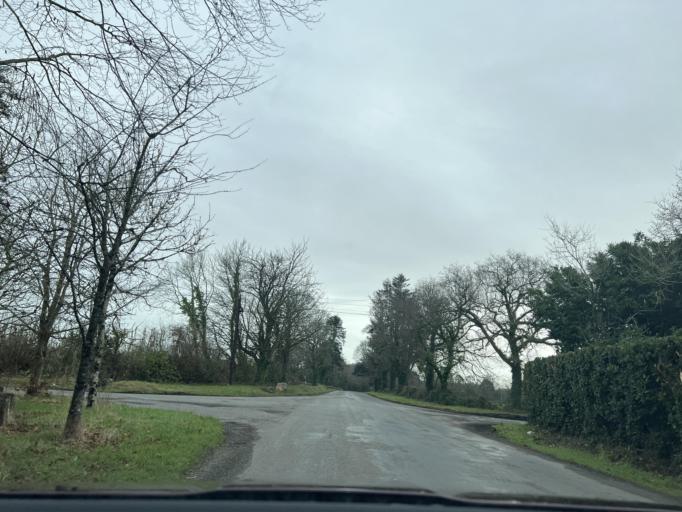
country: IE
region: Leinster
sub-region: Loch Garman
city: Castlebridge
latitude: 52.3836
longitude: -6.5250
